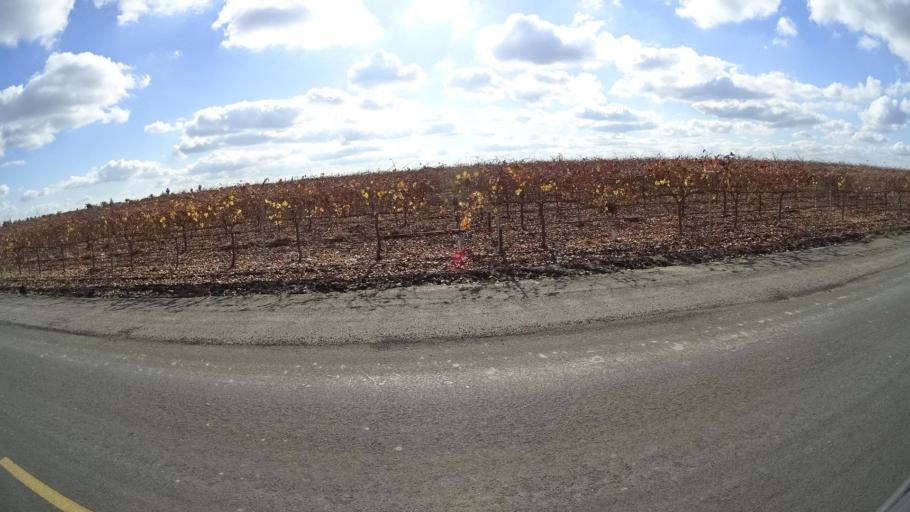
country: US
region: California
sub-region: Kern County
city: McFarland
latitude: 35.6816
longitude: -119.2439
